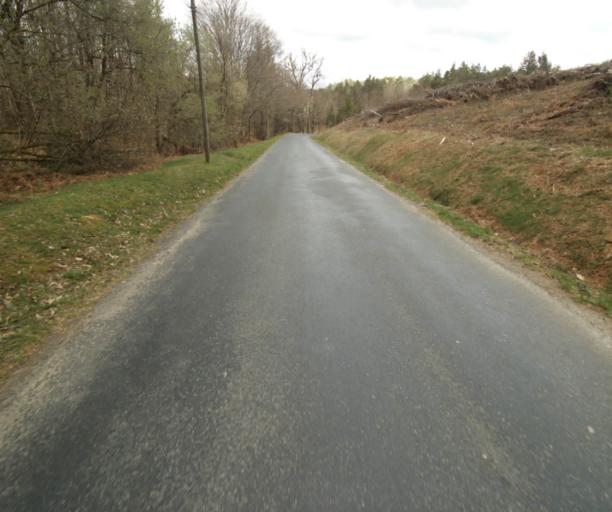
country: FR
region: Limousin
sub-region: Departement de la Correze
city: Correze
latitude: 45.3661
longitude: 1.9298
